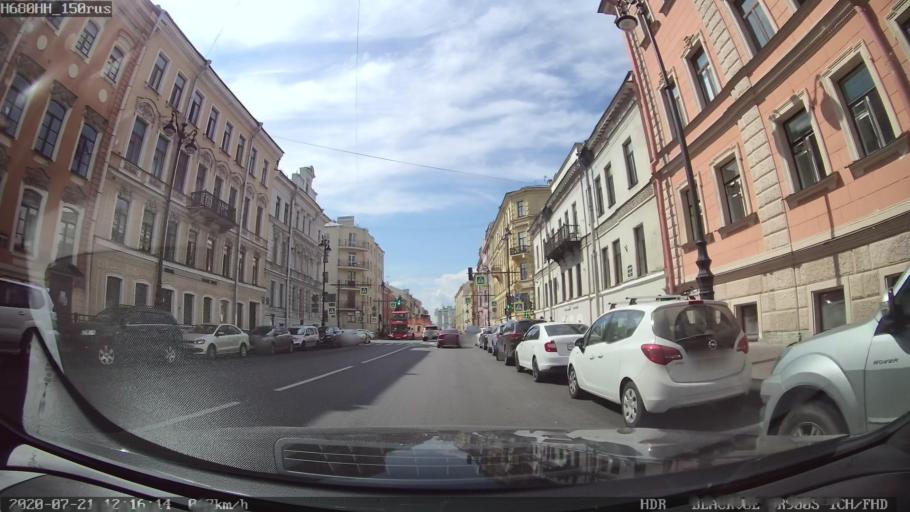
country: RU
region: St.-Petersburg
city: Saint Petersburg
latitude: 59.9434
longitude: 30.3231
